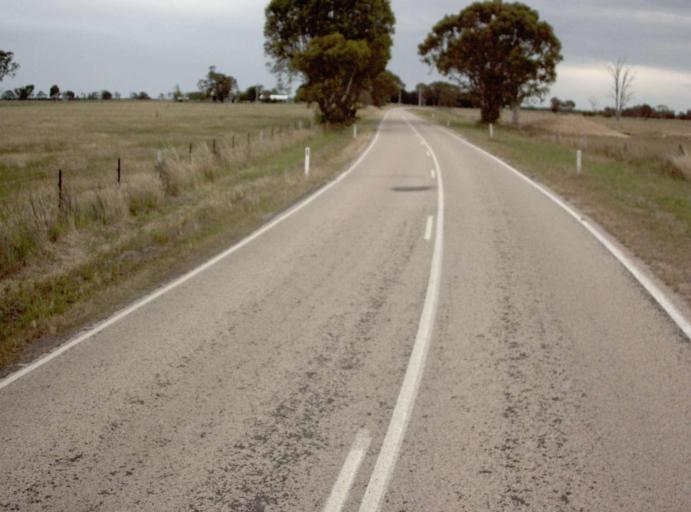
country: AU
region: Victoria
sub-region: East Gippsland
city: Bairnsdale
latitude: -37.9283
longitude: 147.5404
